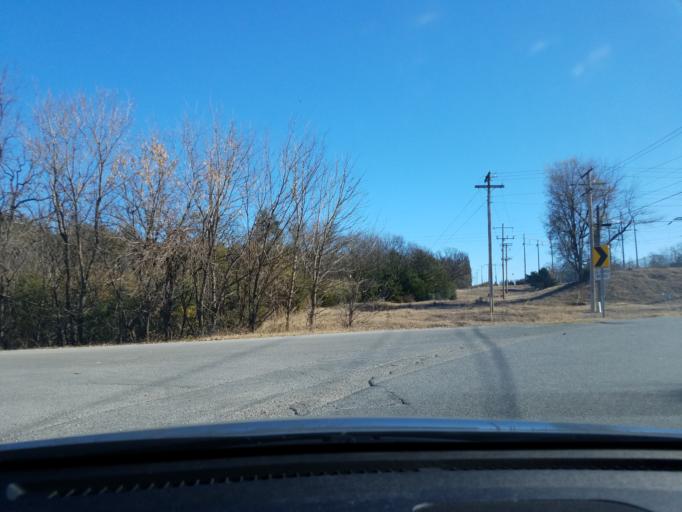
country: US
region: Arkansas
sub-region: Carroll County
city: Berryville
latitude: 36.3780
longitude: -93.5730
